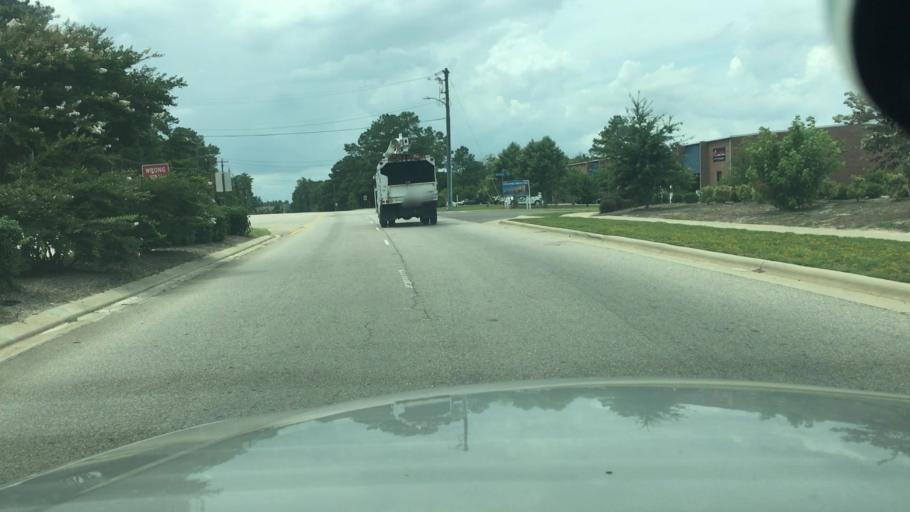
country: US
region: North Carolina
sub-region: Cumberland County
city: Fayetteville
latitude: 34.9967
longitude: -78.8916
